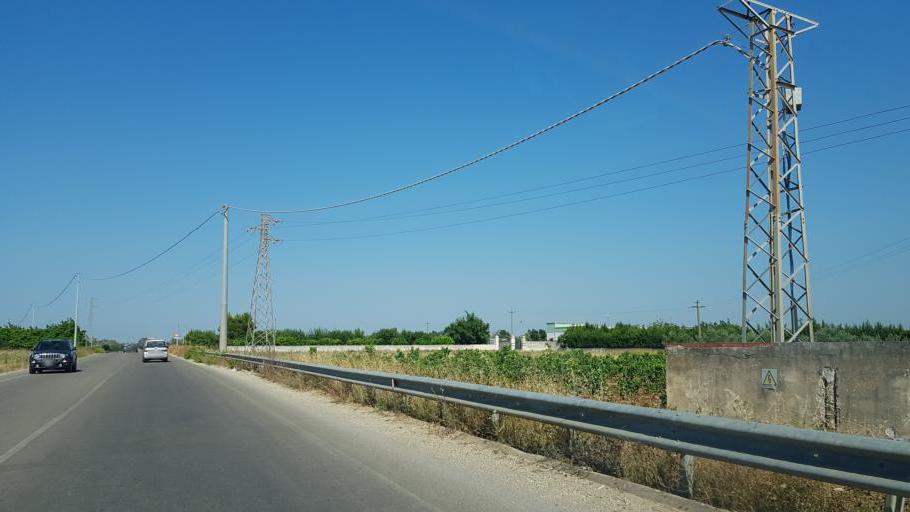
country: IT
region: Apulia
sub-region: Provincia di Lecce
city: Veglie
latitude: 40.3493
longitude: 17.9648
